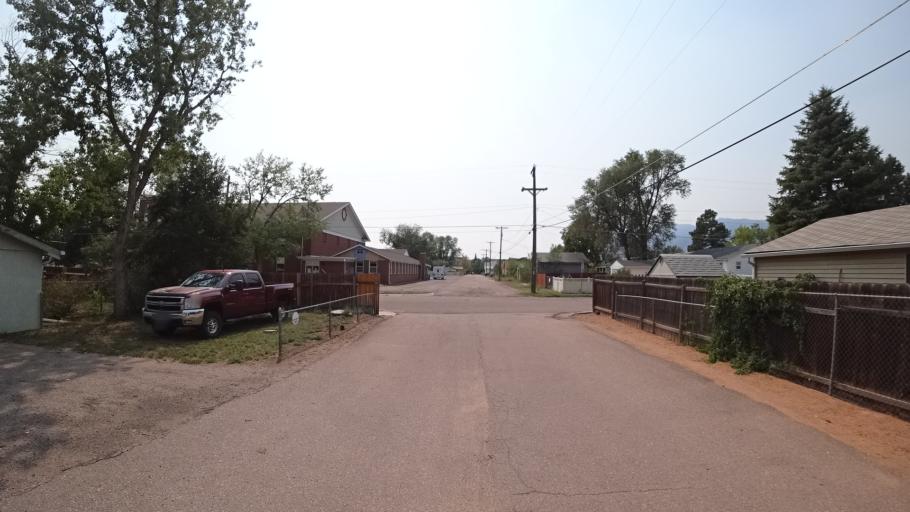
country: US
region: Colorado
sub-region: El Paso County
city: Colorado Springs
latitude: 38.8107
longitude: -104.8185
